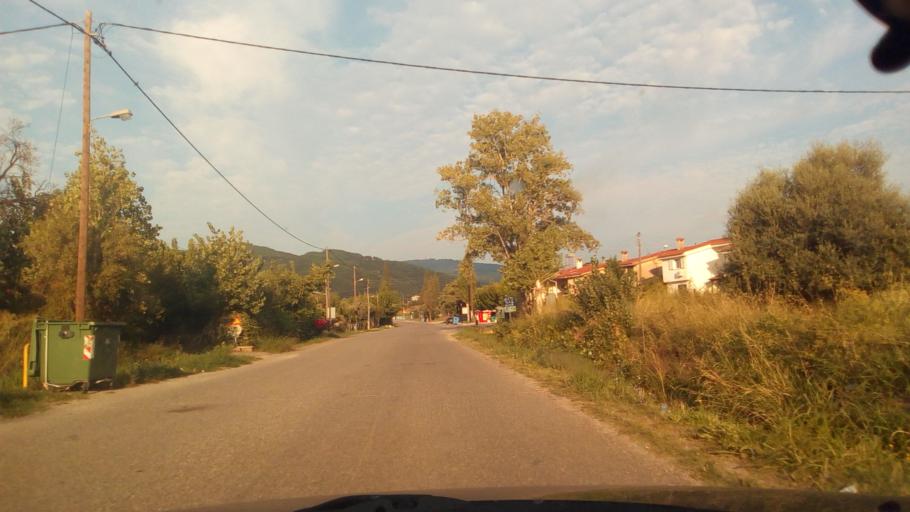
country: GR
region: West Greece
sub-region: Nomos Aitolias kai Akarnanias
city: Nafpaktos
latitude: 38.3965
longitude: 21.8022
